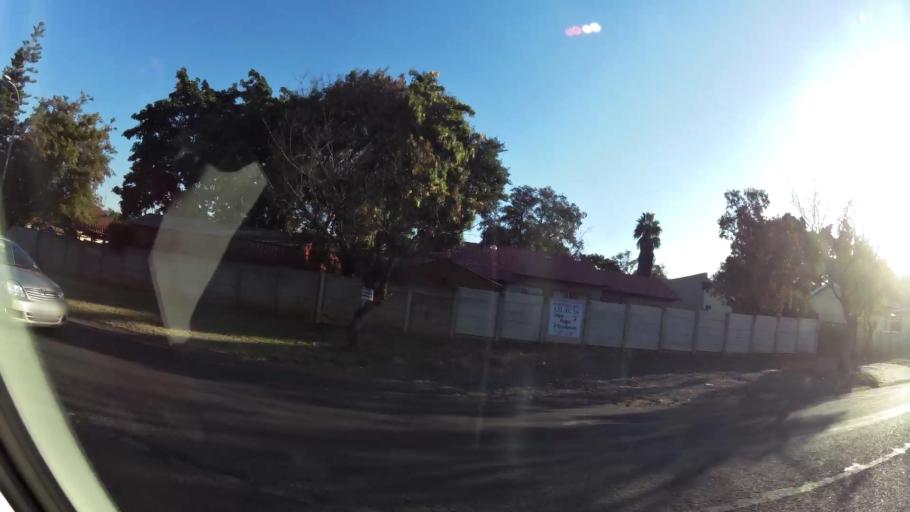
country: ZA
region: North-West
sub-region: Bojanala Platinum District Municipality
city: Rustenburg
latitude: -25.6747
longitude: 27.2122
